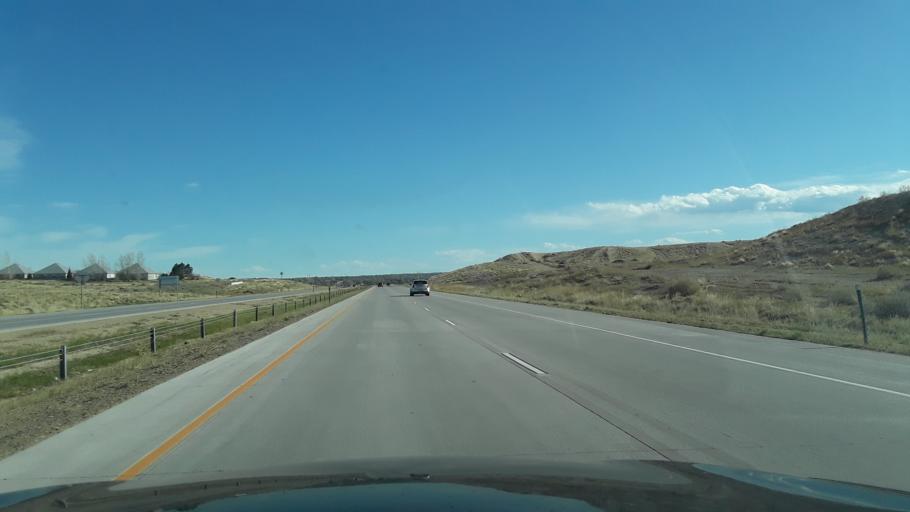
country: US
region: Colorado
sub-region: Pueblo County
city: Pueblo
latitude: 38.2900
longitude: -104.6637
